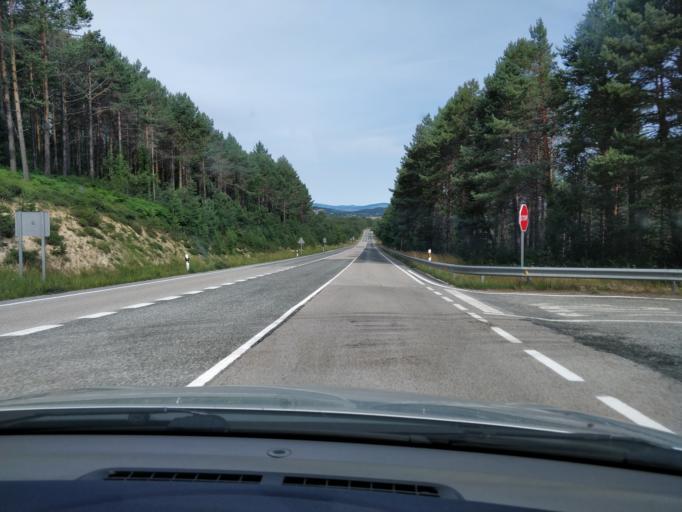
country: ES
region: Cantabria
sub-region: Provincia de Cantabria
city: San Martin de Elines
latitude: 42.9570
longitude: -3.7667
